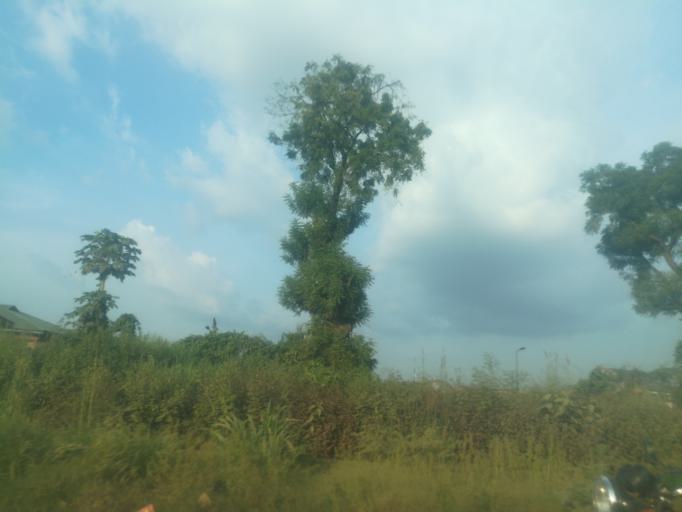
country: NG
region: Ogun
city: Abeokuta
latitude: 7.1699
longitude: 3.2953
